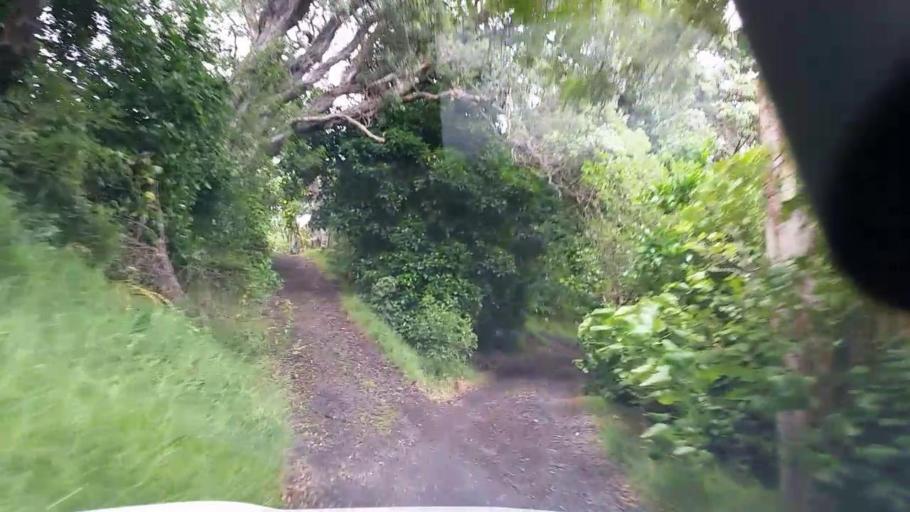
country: NZ
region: Auckland
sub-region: Auckland
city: Muriwai Beach
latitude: -36.9852
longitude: 174.4784
